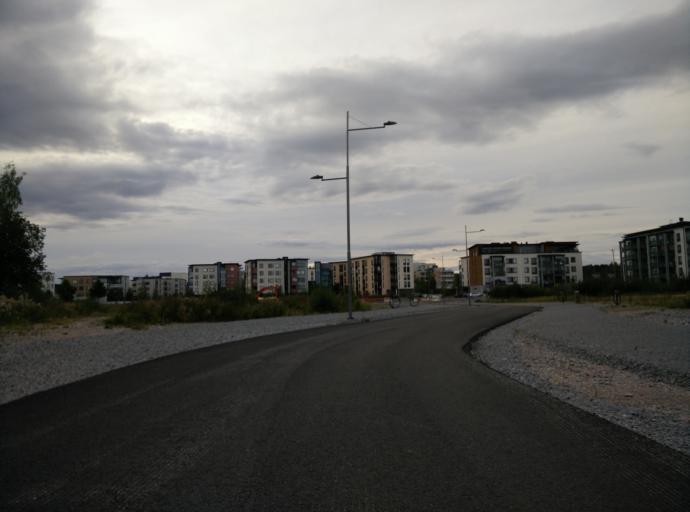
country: FI
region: Haeme
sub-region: Haemeenlinna
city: Haemeenlinna
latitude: 60.9963
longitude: 24.4851
